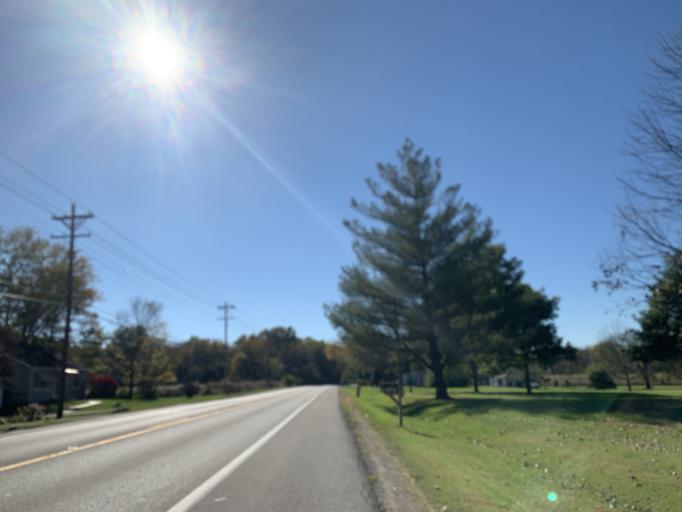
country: US
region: Kentucky
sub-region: Jefferson County
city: Saint Dennis
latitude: 38.2003
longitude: -85.8573
